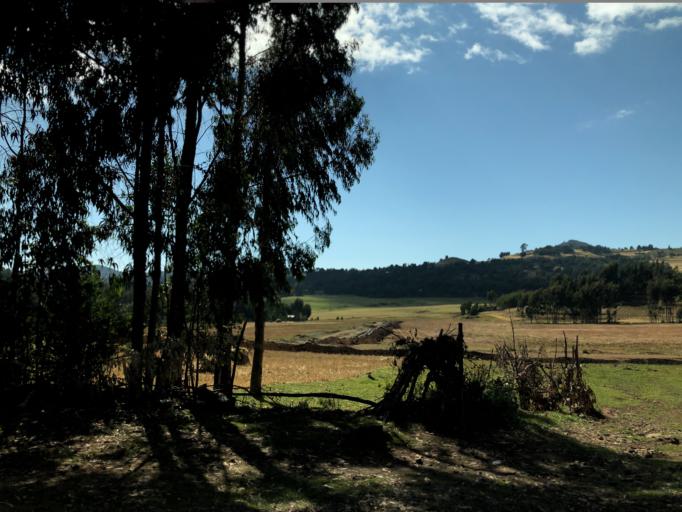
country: ET
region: Amhara
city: Debre Tabor
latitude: 11.7172
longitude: 38.4540
